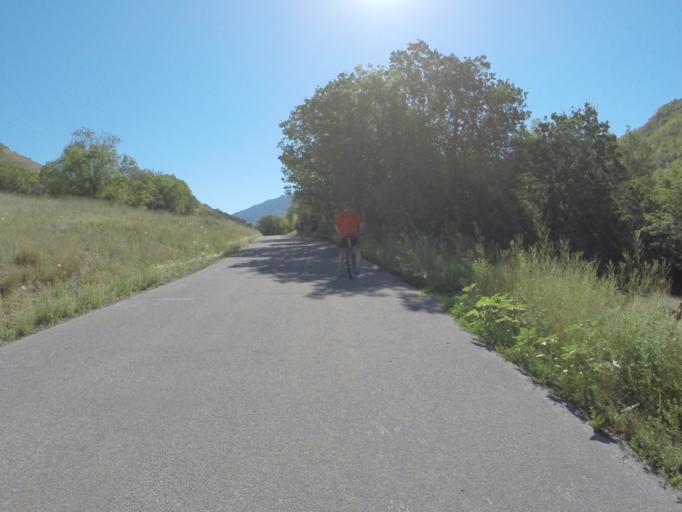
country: US
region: Utah
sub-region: Salt Lake County
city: Salt Lake City
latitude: 40.8048
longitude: -111.8645
